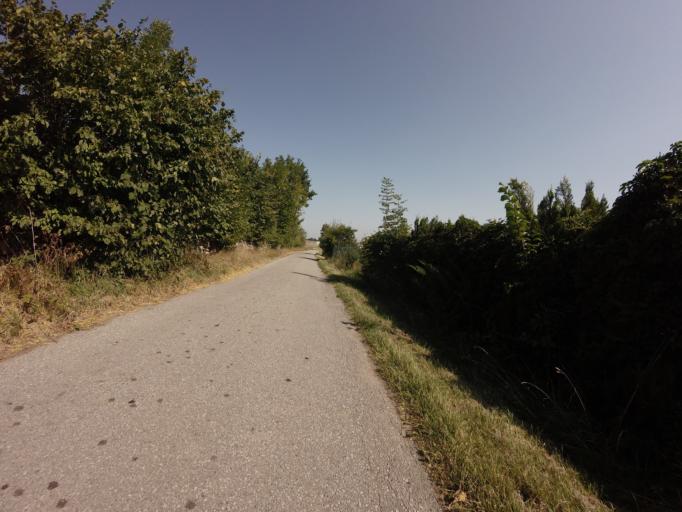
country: CZ
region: Jihocesky
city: Kamenny Ujezd
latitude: 48.8756
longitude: 14.3828
